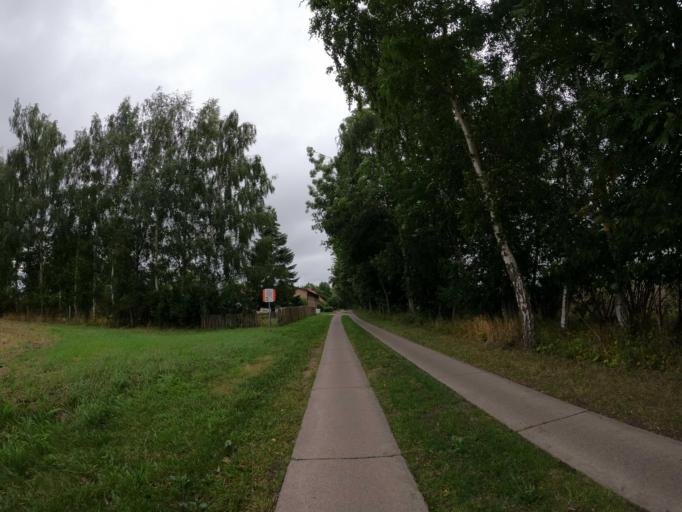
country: DE
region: Mecklenburg-Vorpommern
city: Garz
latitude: 54.3016
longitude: 13.3349
